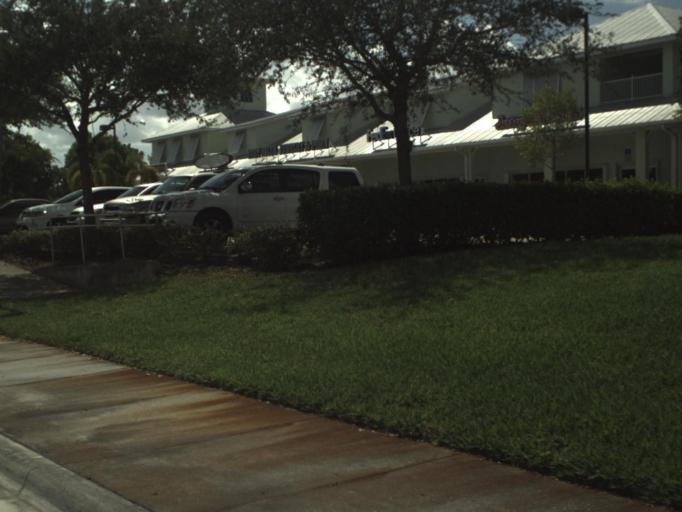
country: US
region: Florida
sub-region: Saint Lucie County
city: Port Saint Lucie
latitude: 27.2741
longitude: -80.3539
